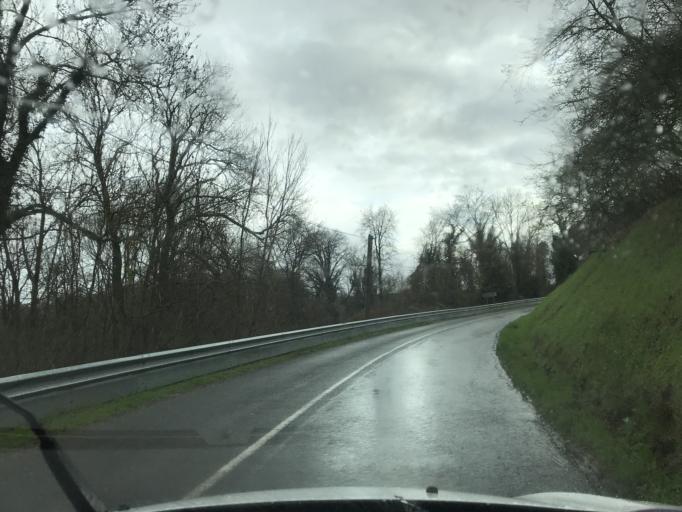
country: FR
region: Picardie
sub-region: Departement de l'Aisne
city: Billy-sur-Aisne
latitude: 49.3467
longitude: 3.3861
